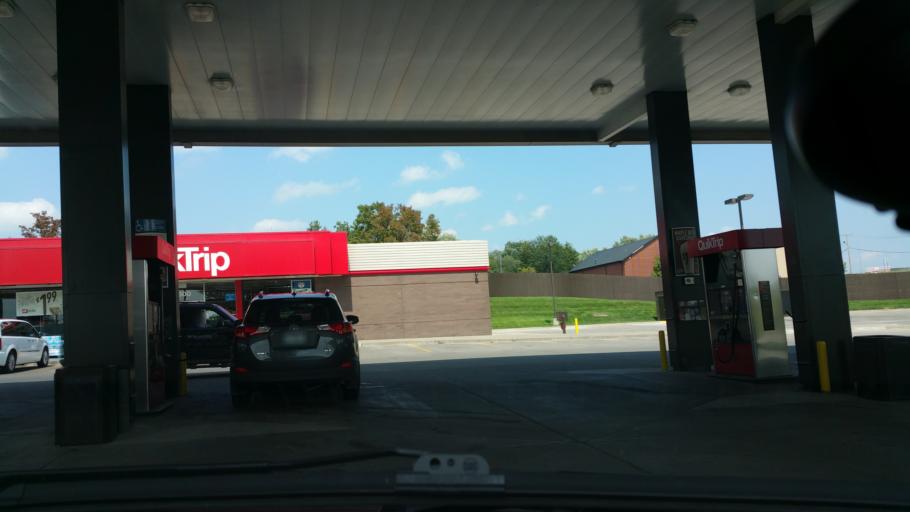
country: US
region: Missouri
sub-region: Clay County
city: Pleasant Valley
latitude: 39.2166
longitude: -94.4767
